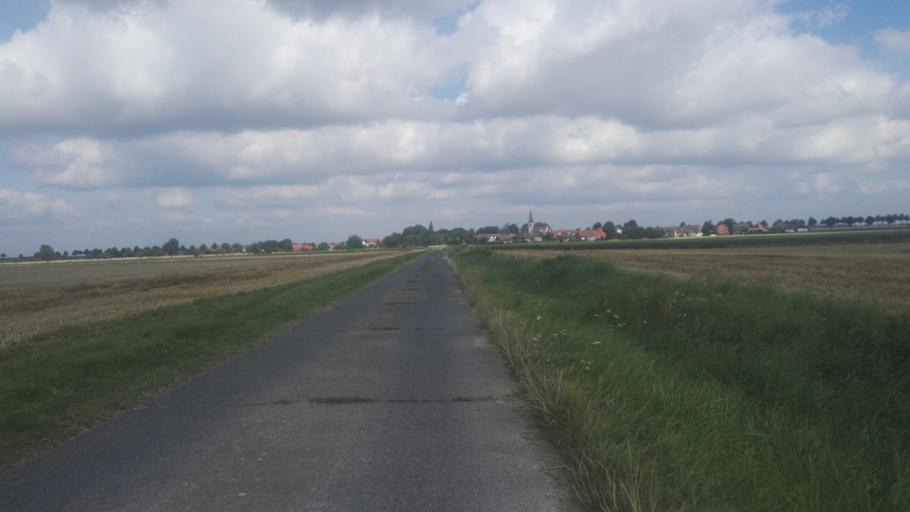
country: DE
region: Lower Saxony
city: Schellerten
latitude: 52.1630
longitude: 10.0461
